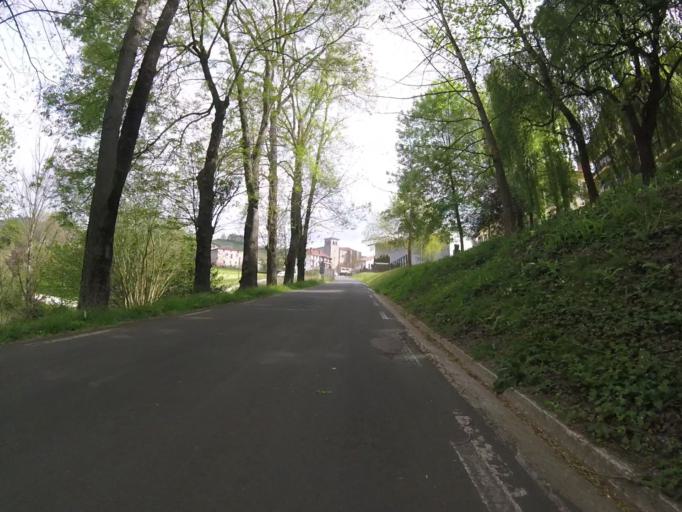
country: ES
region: Basque Country
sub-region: Provincia de Guipuzcoa
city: Zizurkil
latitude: 43.1981
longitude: -2.0755
